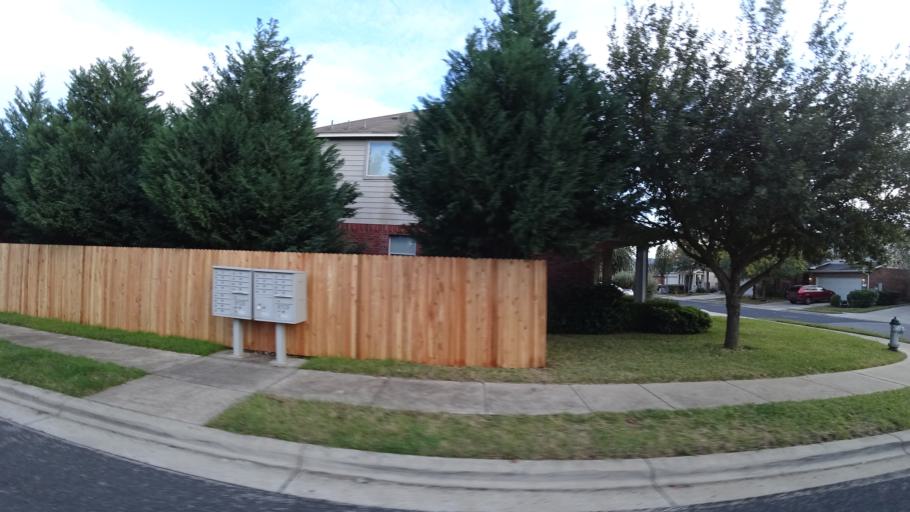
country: US
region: Texas
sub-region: Williamson County
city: Brushy Creek
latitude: 30.4972
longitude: -97.7396
